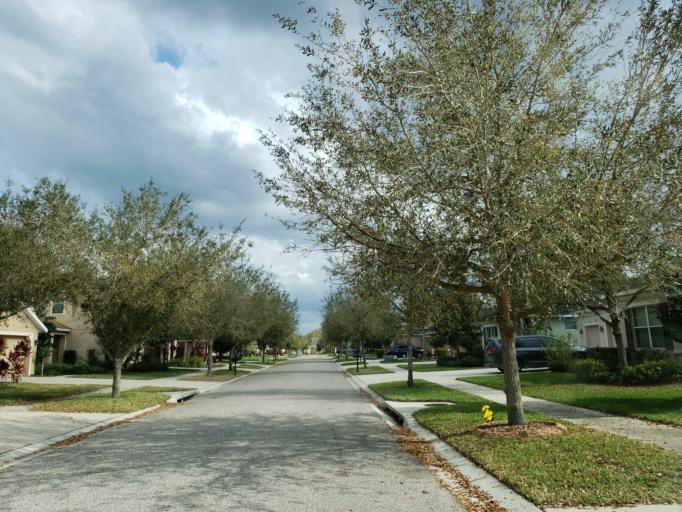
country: US
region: Florida
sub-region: Hillsborough County
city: Fish Hawk
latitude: 27.8368
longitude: -82.2081
